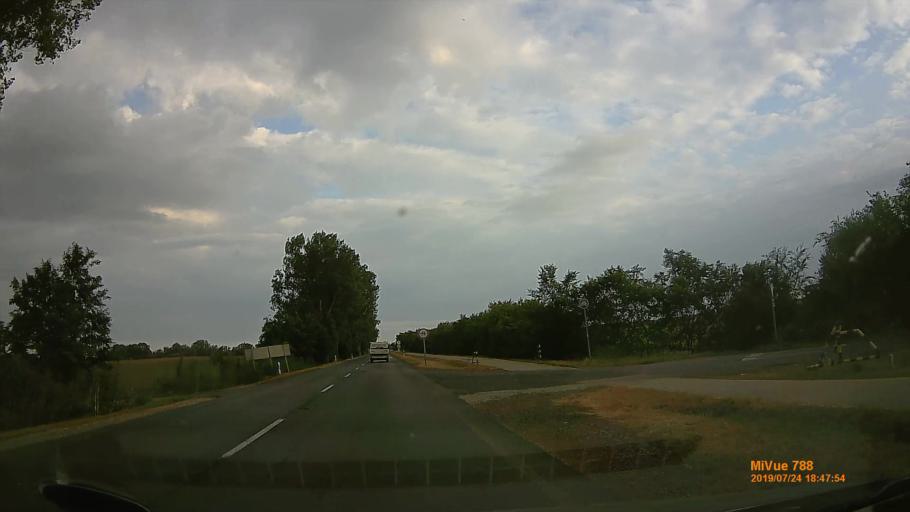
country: HU
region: Szabolcs-Szatmar-Bereg
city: Tiszanagyfalu
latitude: 48.0889
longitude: 21.4965
